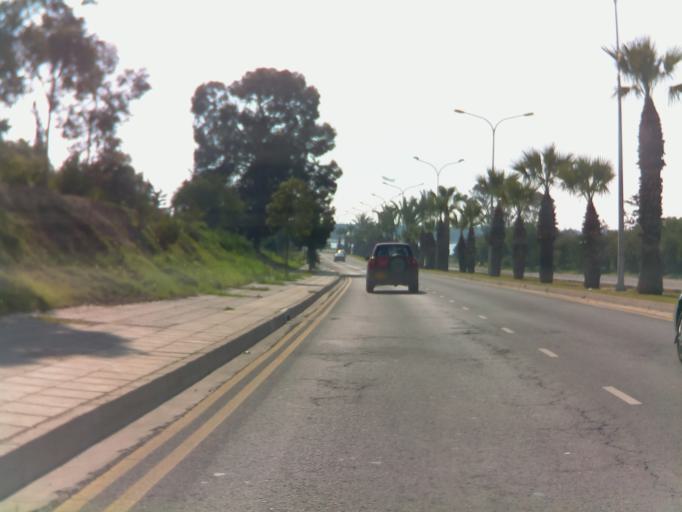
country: CY
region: Larnaka
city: Larnaca
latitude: 34.8996
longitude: 33.6304
